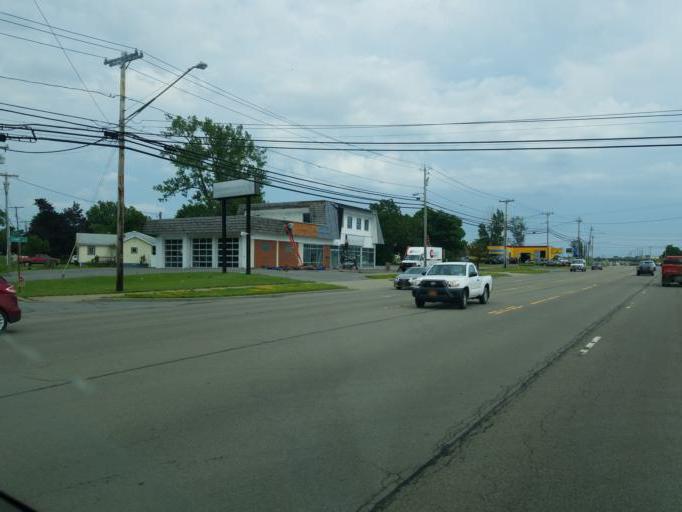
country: US
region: New York
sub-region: Erie County
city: Hamburg
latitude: 42.7472
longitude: -78.8527
